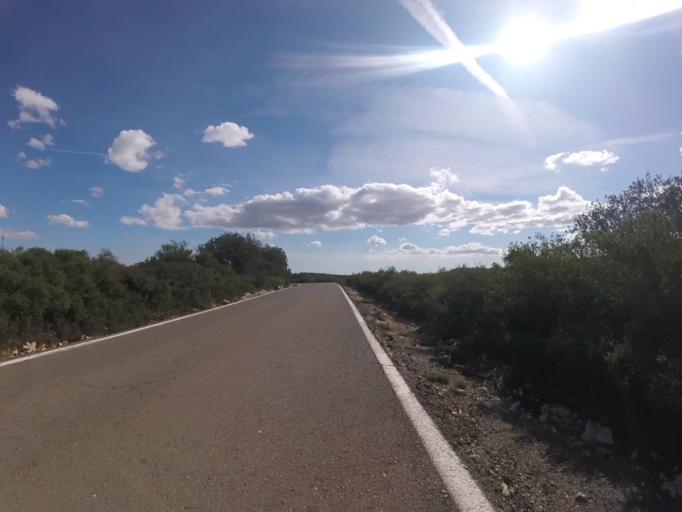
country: ES
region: Valencia
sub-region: Provincia de Castello
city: Albocasser
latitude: 40.3981
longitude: 0.0877
